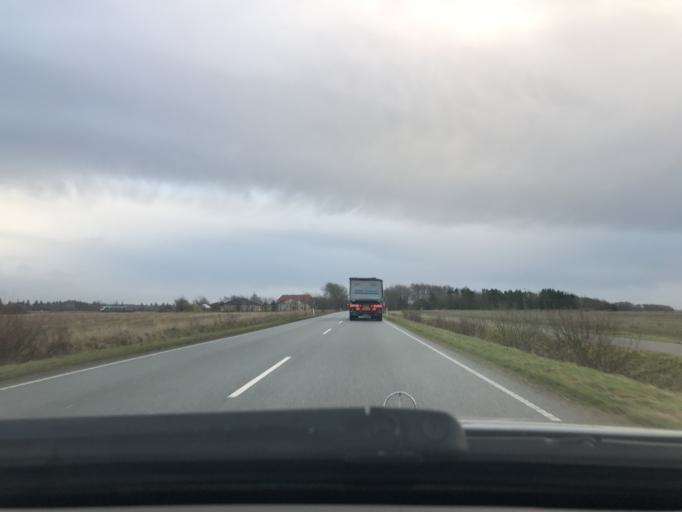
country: DK
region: South Denmark
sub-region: Tonder Kommune
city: Sherrebek
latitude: 55.1774
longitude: 8.7456
